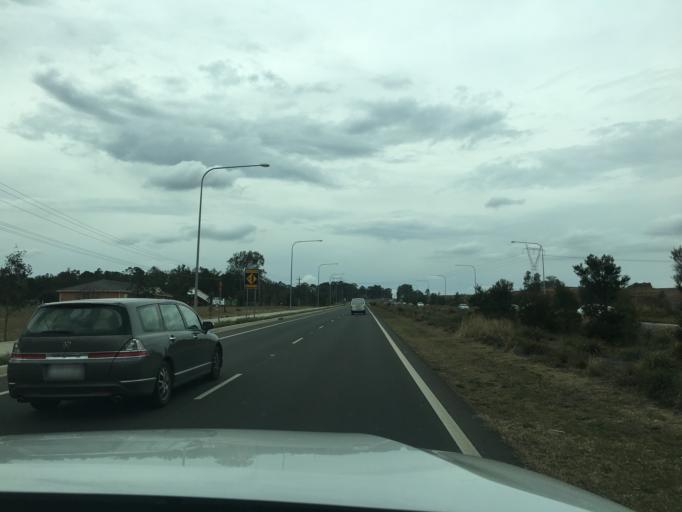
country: AU
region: New South Wales
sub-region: Campbelltown Municipality
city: Denham Court
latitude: -33.9927
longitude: 150.7884
